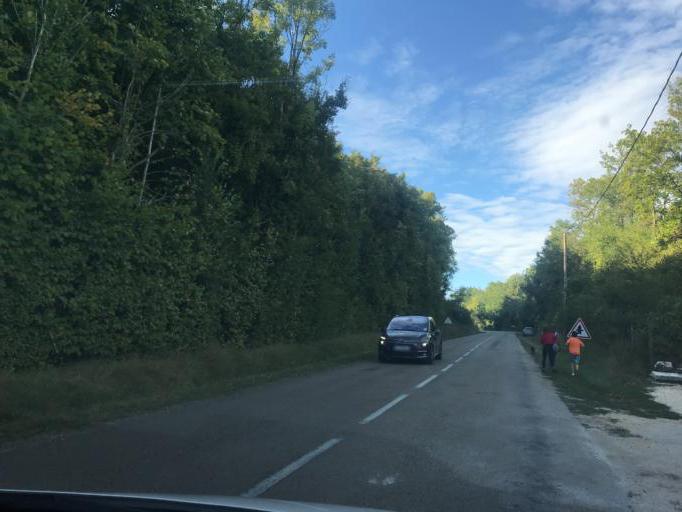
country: FR
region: Bourgogne
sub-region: Departement de l'Yonne
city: Fontenailles
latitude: 47.5471
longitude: 3.4262
